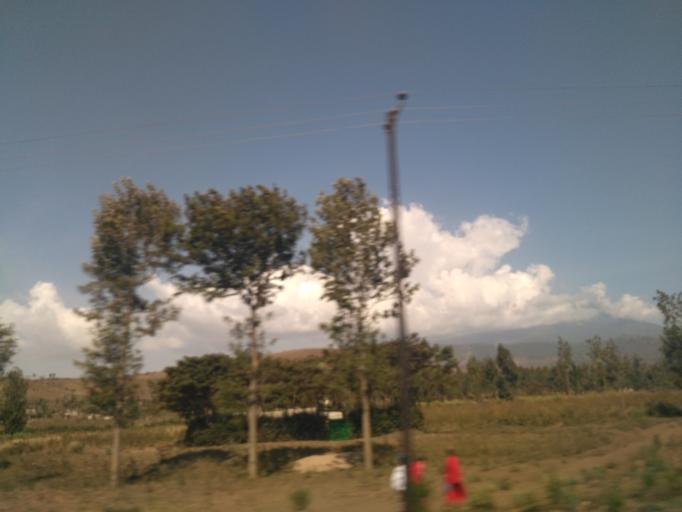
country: TZ
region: Arusha
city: Arusha
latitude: -3.2277
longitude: 36.6071
